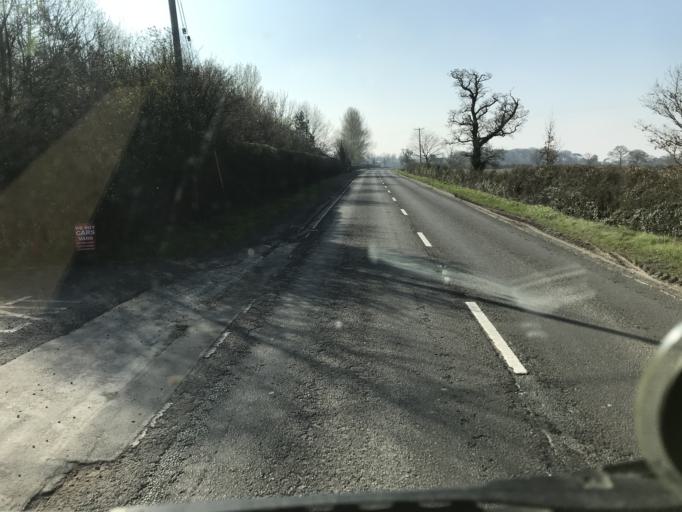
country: GB
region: England
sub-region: Cheshire West and Chester
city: Waverton
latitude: 53.1505
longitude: -2.8118
